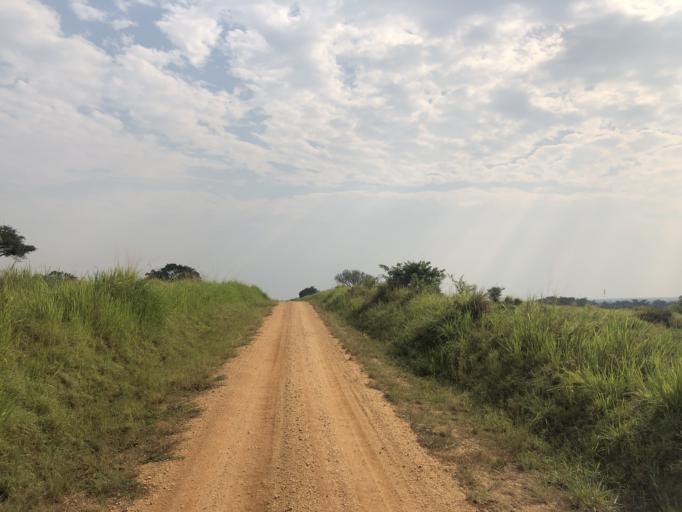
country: UG
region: Western Region
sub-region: Mitoma District
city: Mitoma
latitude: -0.5263
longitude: 29.7970
